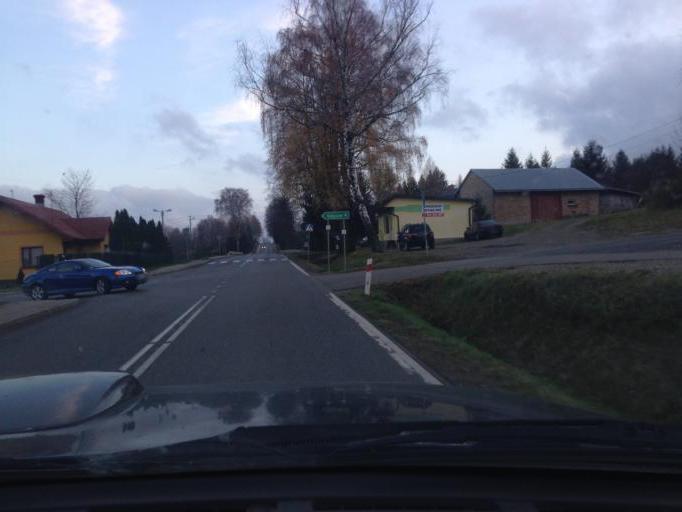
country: PL
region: Subcarpathian Voivodeship
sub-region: Powiat jasielski
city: Osiek Jasielski
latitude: 49.6424
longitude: 21.5176
